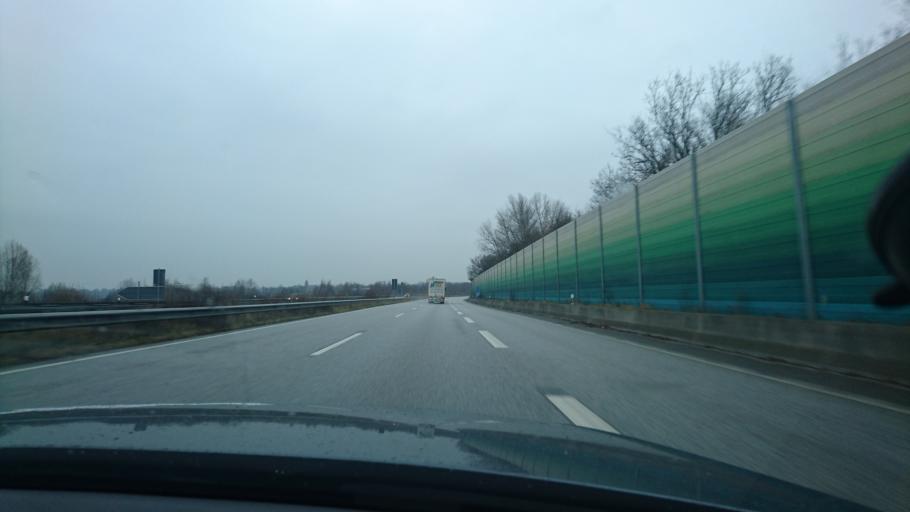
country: DE
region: Schleswig-Holstein
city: Oldenburg in Holstein
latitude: 54.2883
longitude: 10.8734
